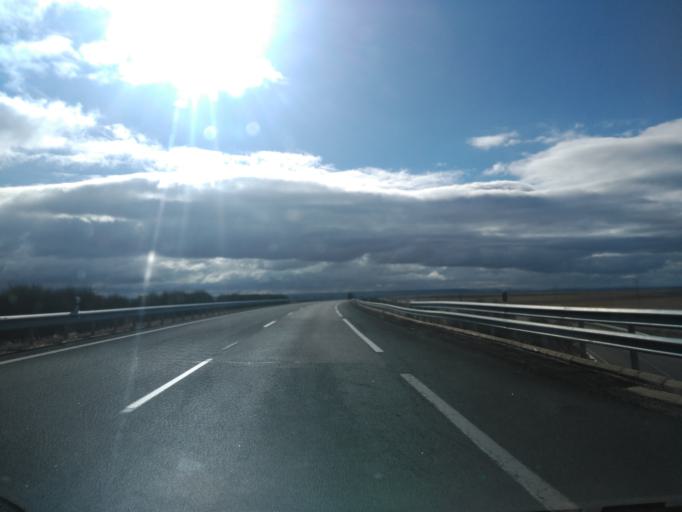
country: ES
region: Castille and Leon
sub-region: Provincia de Palencia
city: Marcilla de Campos
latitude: 42.3052
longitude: -4.3987
